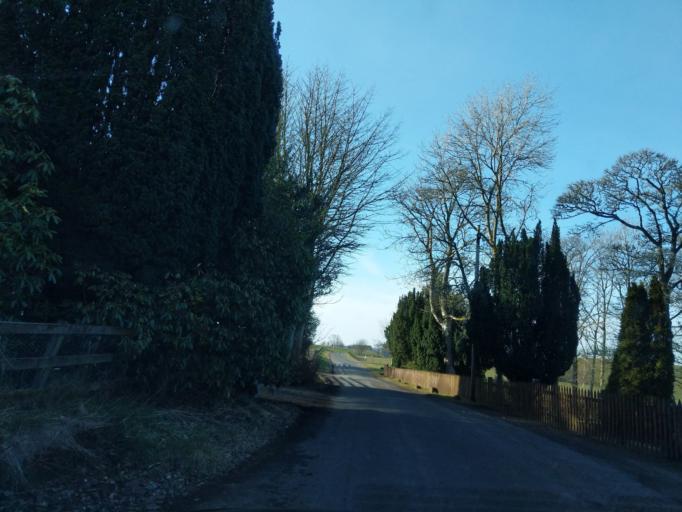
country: GB
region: Scotland
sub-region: The Scottish Borders
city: West Linton
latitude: 55.7093
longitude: -3.4374
